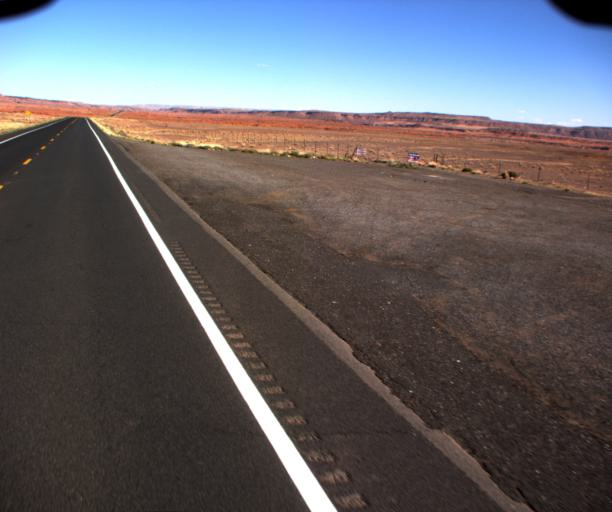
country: US
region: Arizona
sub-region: Coconino County
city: Tuba City
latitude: 36.0969
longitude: -111.3525
